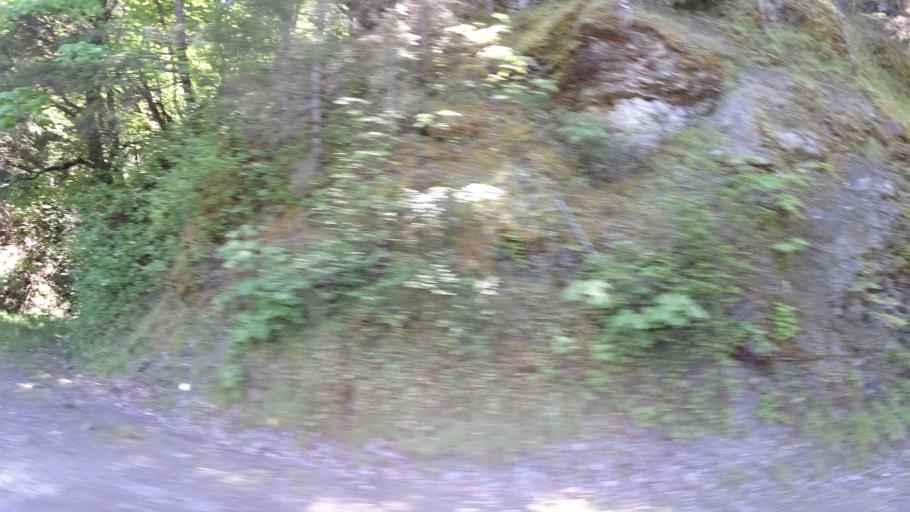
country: US
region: California
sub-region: Humboldt County
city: Willow Creek
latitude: 40.8729
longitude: -123.5320
